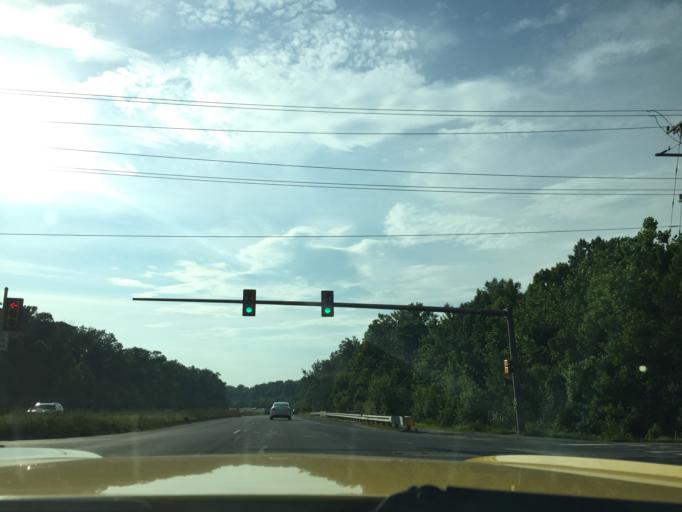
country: US
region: Virginia
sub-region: Fairfax County
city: Fort Belvoir
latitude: 38.7188
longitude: -77.1681
